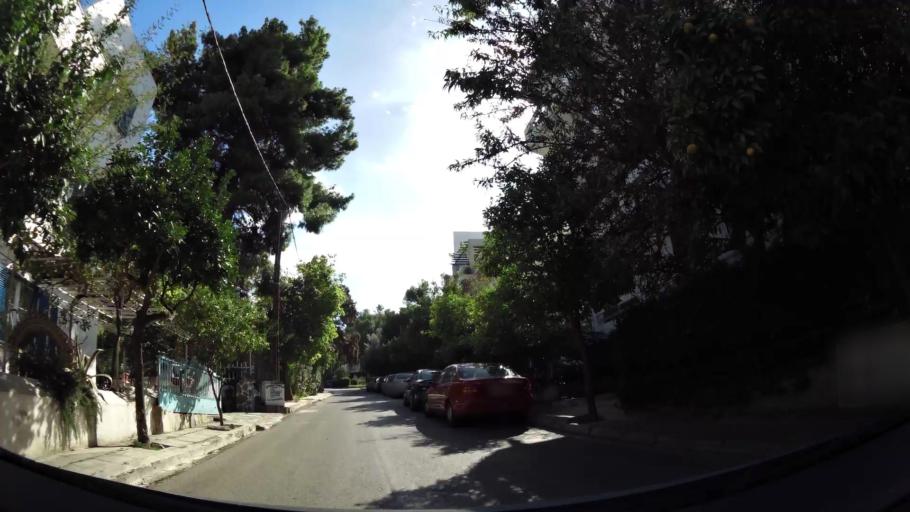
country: GR
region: Attica
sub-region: Nomarchia Athinas
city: Neo Psychiko
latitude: 38.0066
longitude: 23.7788
